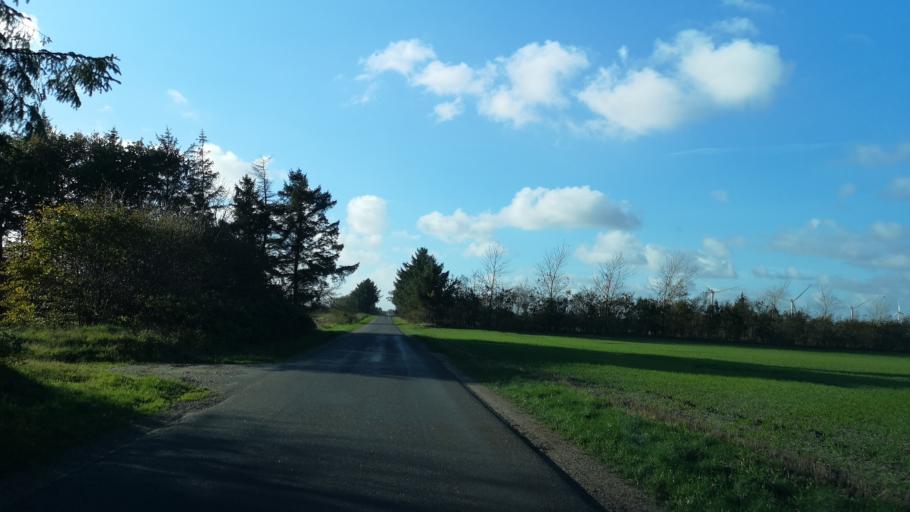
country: DK
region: Central Jutland
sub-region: Ringkobing-Skjern Kommune
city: Skjern
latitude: 55.8373
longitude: 8.3528
